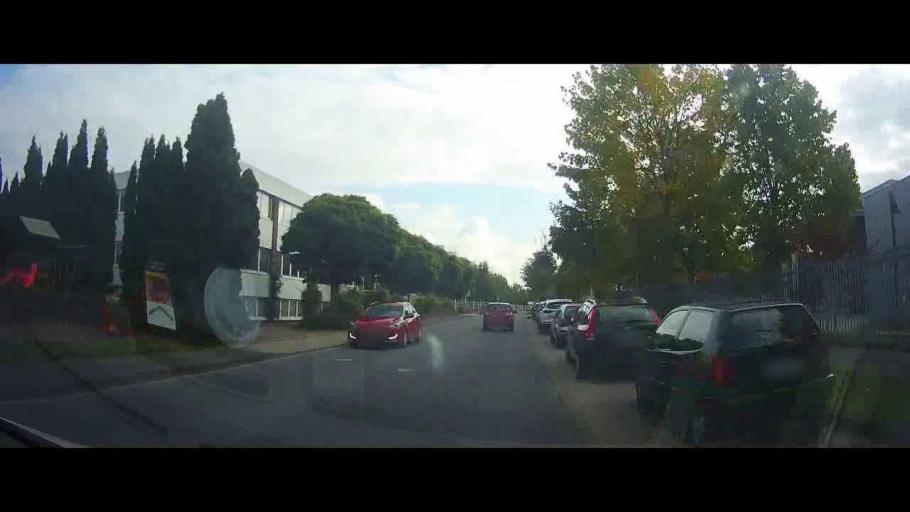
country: DE
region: Lower Saxony
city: Goettingen
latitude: 51.5541
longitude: 9.8918
